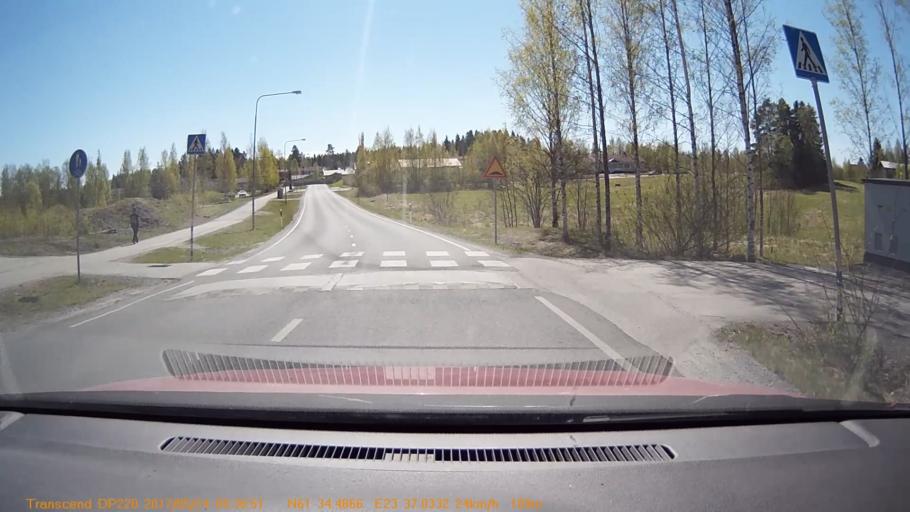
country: FI
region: Pirkanmaa
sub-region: Tampere
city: Yloejaervi
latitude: 61.5748
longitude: 23.6174
